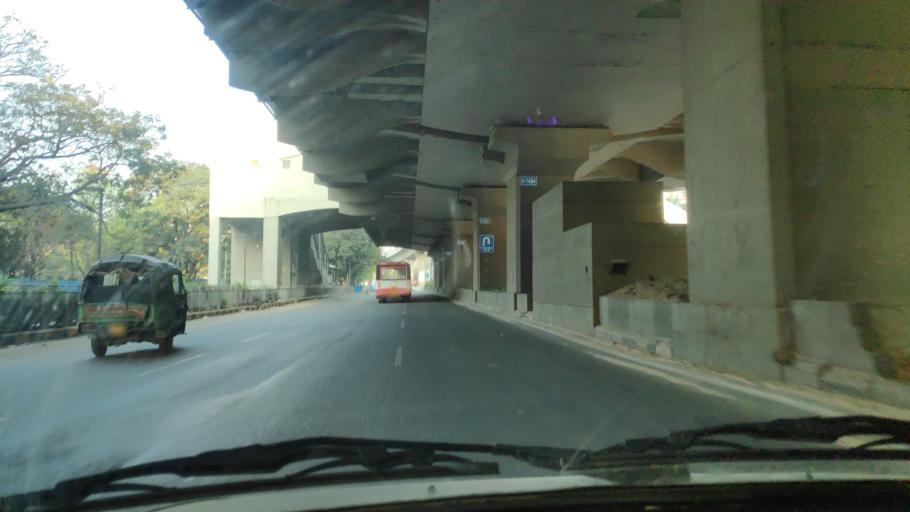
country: IN
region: Telangana
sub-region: Rangareddi
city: Gaddi Annaram
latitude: 17.3709
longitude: 78.5122
